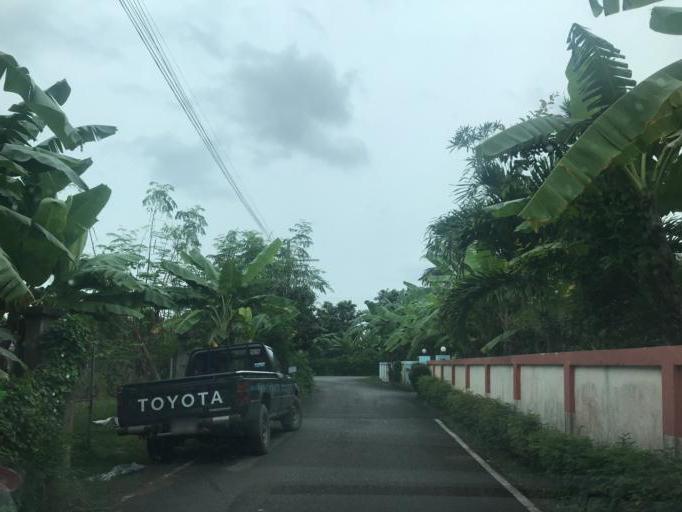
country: TH
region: Chiang Mai
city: Saraphi
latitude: 18.6958
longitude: 99.0219
